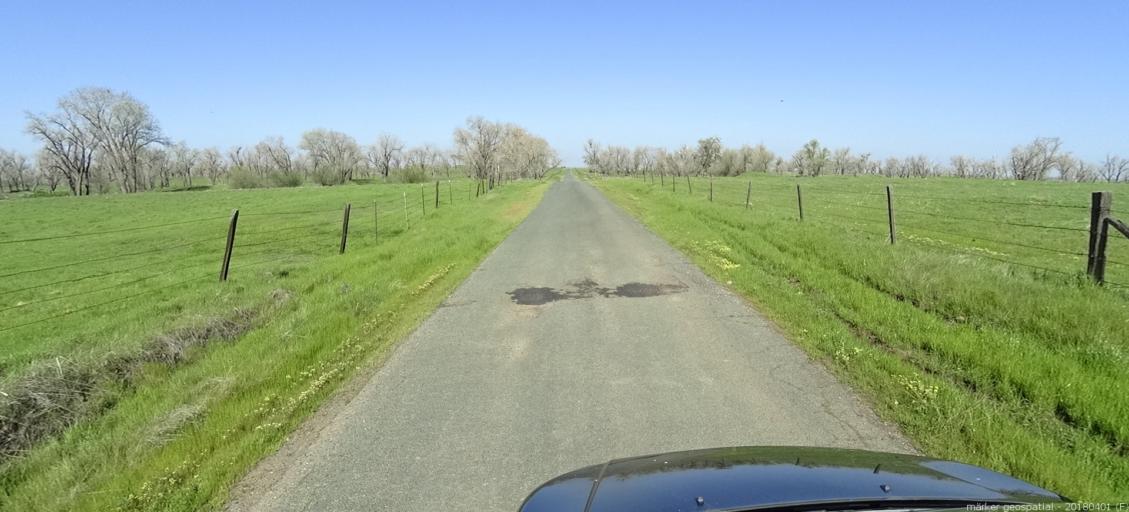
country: US
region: California
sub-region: Sacramento County
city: Rancho Murieta
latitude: 38.4580
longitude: -121.1058
